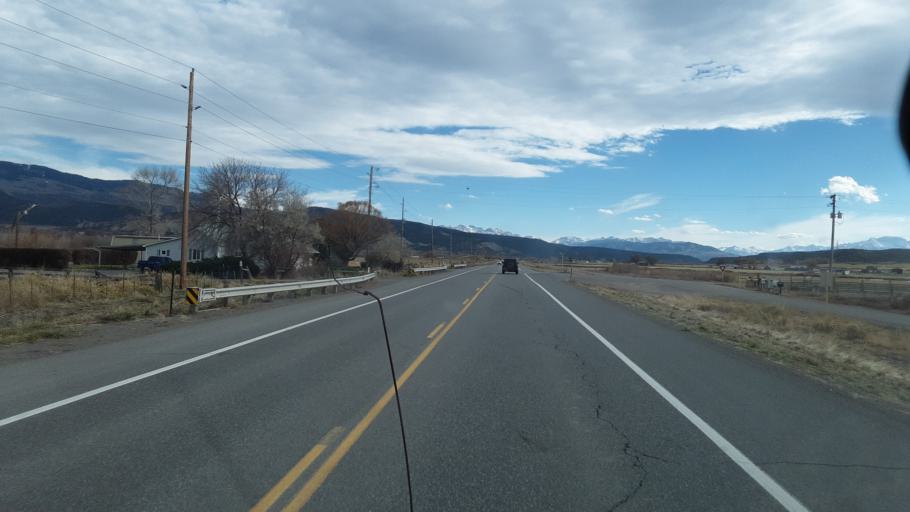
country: US
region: Colorado
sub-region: Montrose County
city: Montrose
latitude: 38.3561
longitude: -107.7999
